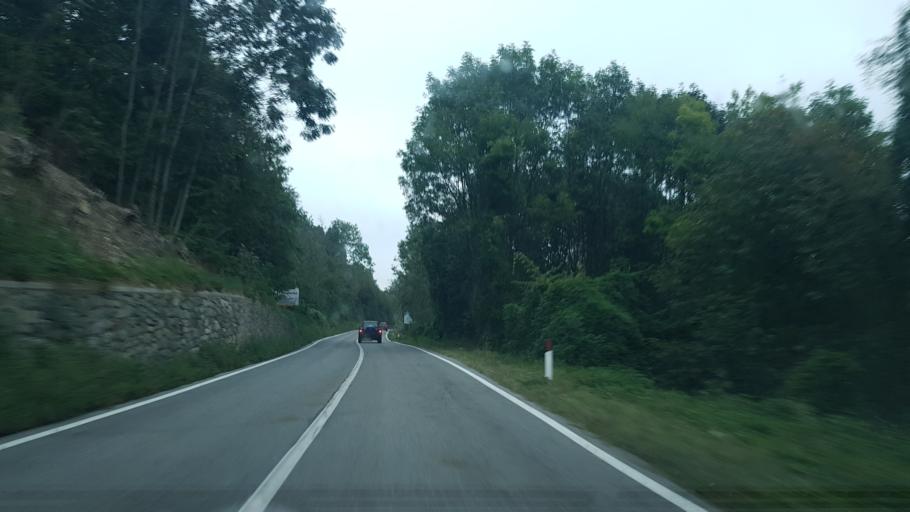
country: IT
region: Piedmont
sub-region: Provincia di Cuneo
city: Frabosa Sottana
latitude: 44.3100
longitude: 7.8026
